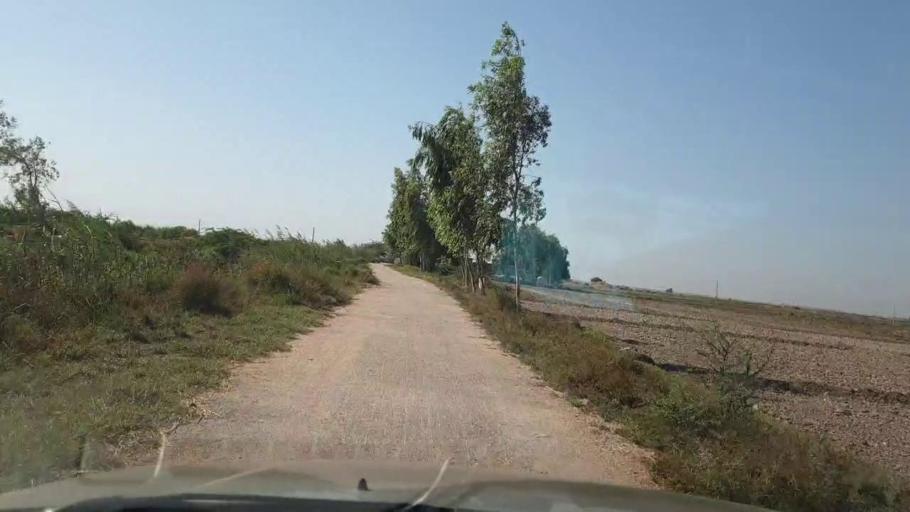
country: PK
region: Sindh
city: Thatta
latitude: 24.7214
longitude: 67.9213
